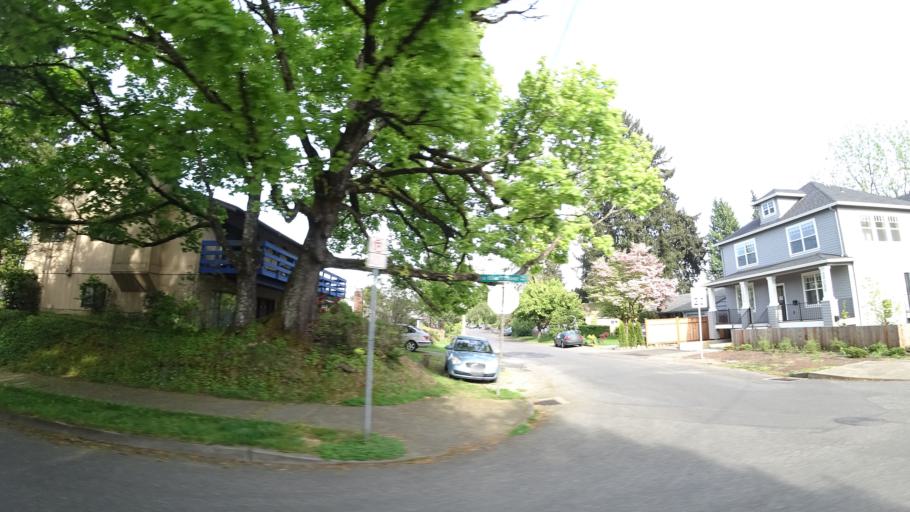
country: US
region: Oregon
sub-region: Clackamas County
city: Milwaukie
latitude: 45.4658
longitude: -122.6226
